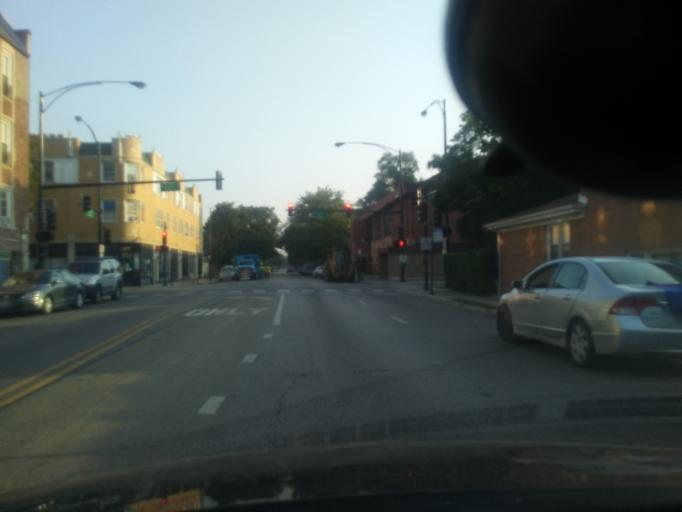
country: US
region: Illinois
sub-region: Cook County
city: Lincolnwood
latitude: 42.0081
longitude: -87.6997
